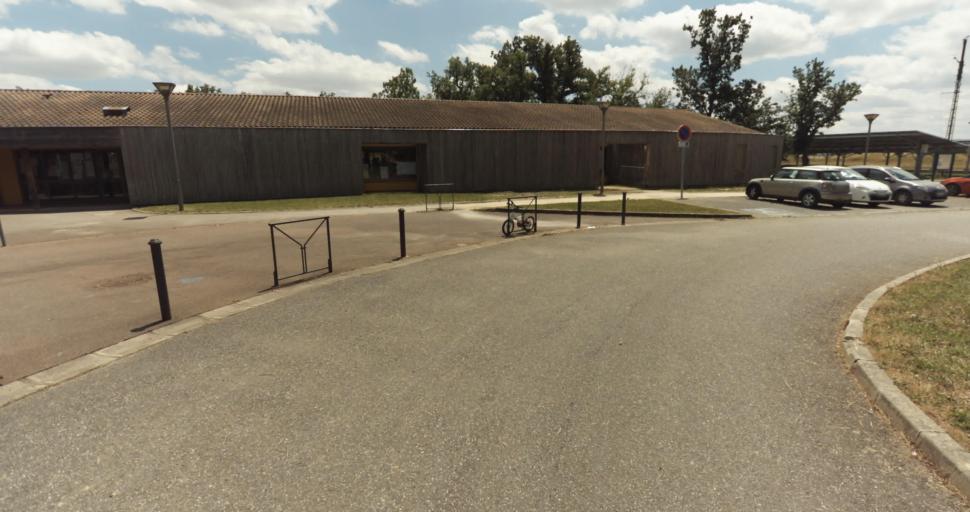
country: FR
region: Midi-Pyrenees
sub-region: Departement de la Haute-Garonne
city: Fontenilles
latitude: 43.5355
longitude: 1.1931
